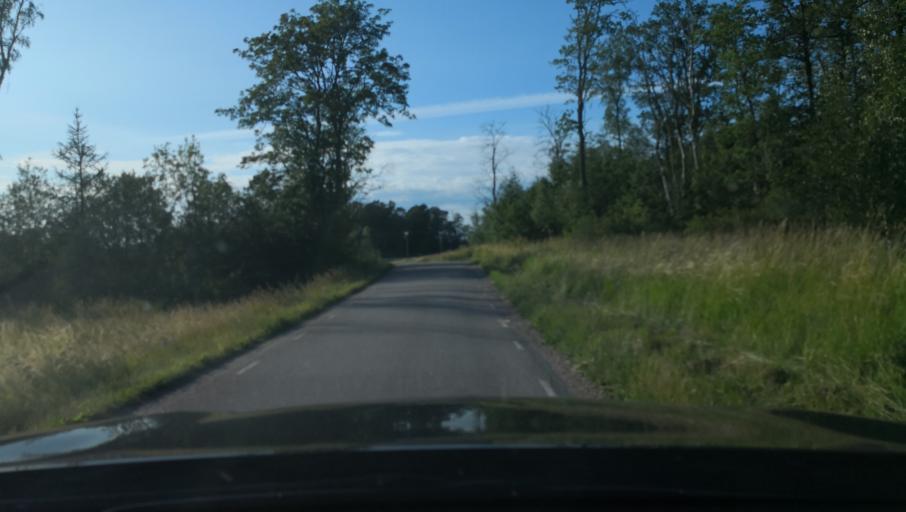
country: SE
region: Uppsala
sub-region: Uppsala Kommun
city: Vattholma
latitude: 59.9173
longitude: 17.8428
